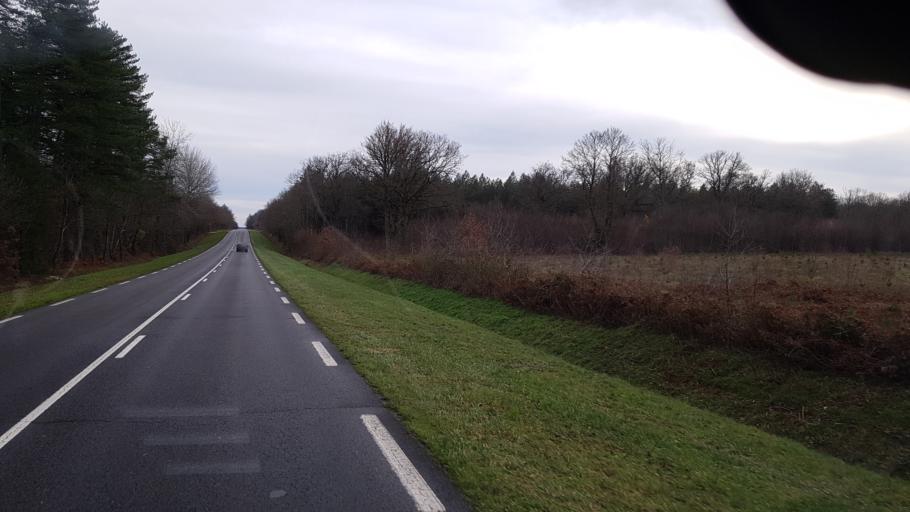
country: FR
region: Centre
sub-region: Departement du Loir-et-Cher
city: Lamotte-Beuvron
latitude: 47.6259
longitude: 2.0087
